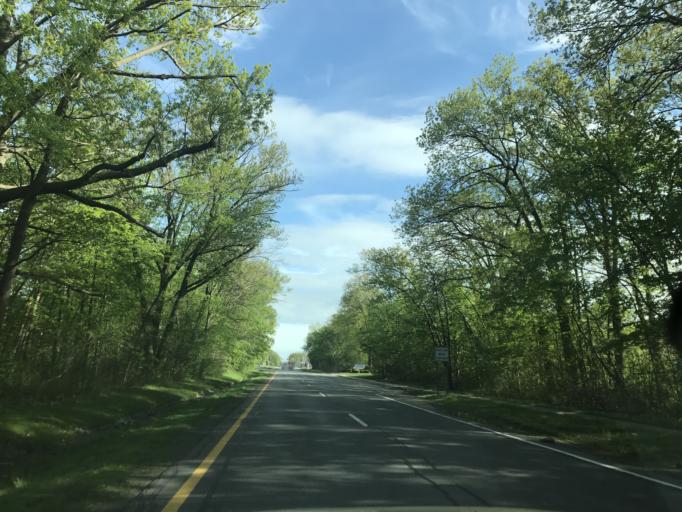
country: US
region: Michigan
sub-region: Wayne County
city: Riverview
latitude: 42.1608
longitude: -83.1890
